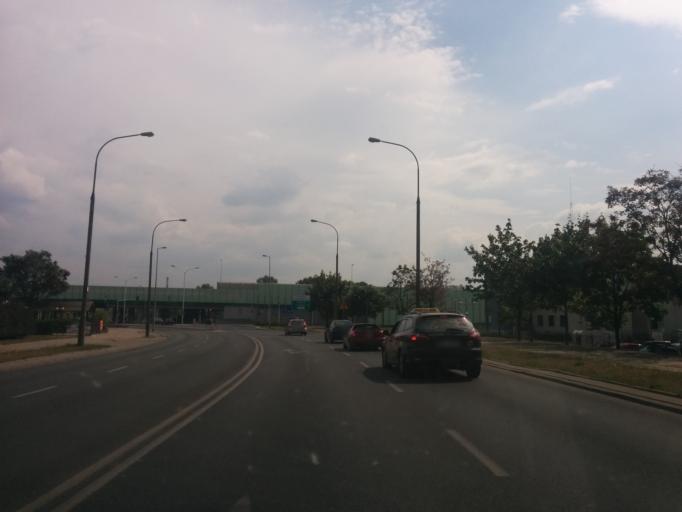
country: PL
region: Masovian Voivodeship
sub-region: Warszawa
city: Bialoleka
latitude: 52.3140
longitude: 20.9632
